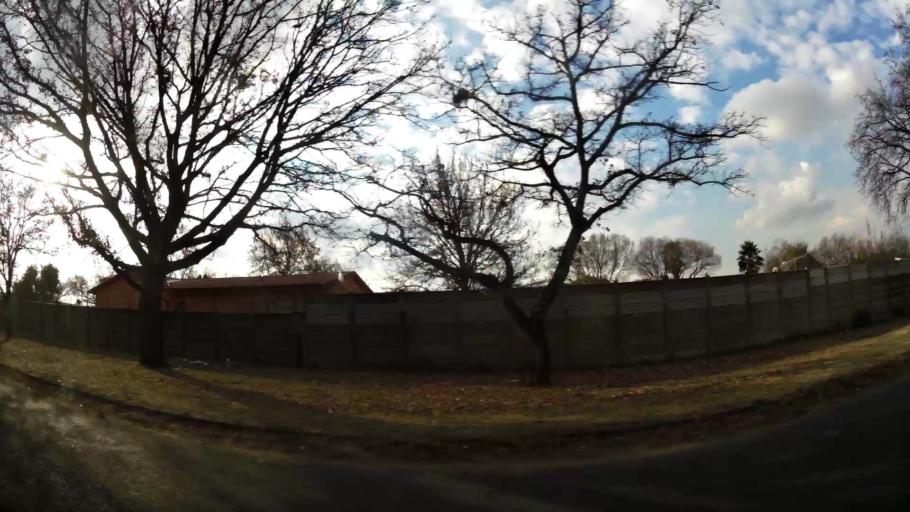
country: ZA
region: Orange Free State
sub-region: Fezile Dabi District Municipality
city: Sasolburg
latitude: -26.8269
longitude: 27.8199
